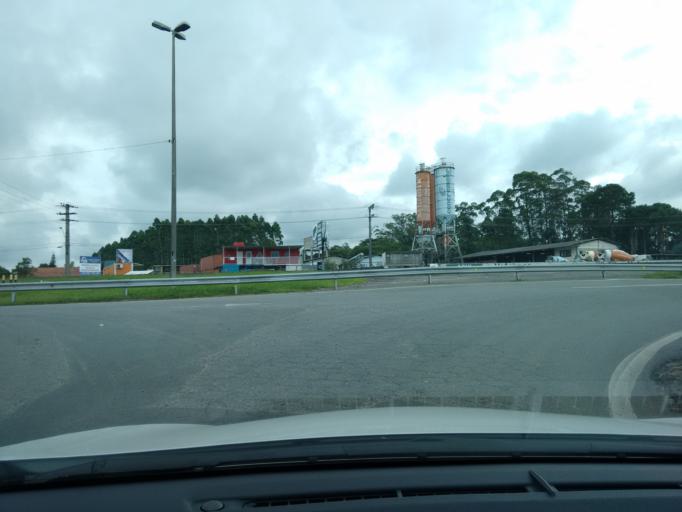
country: BR
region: Santa Catarina
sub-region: Penha
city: Penha
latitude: -26.7624
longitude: -48.6861
